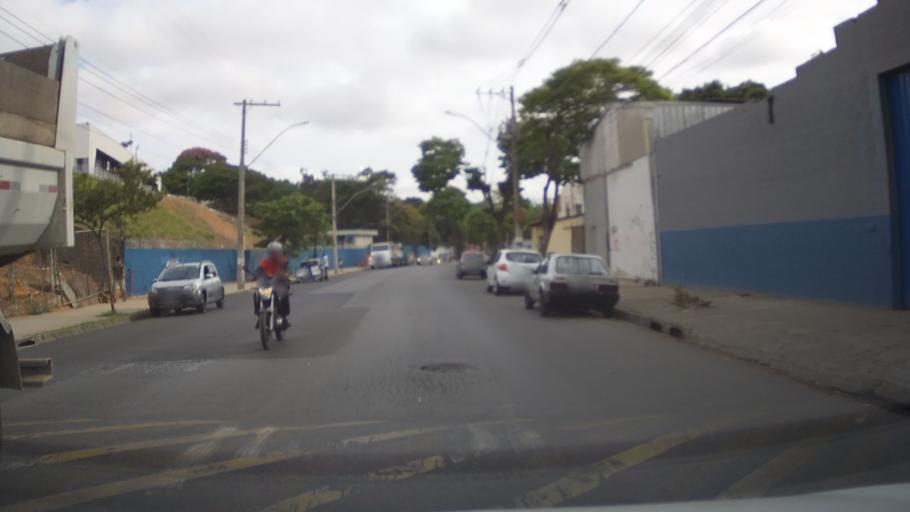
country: BR
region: Minas Gerais
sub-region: Belo Horizonte
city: Belo Horizonte
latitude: -19.8238
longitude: -43.9564
